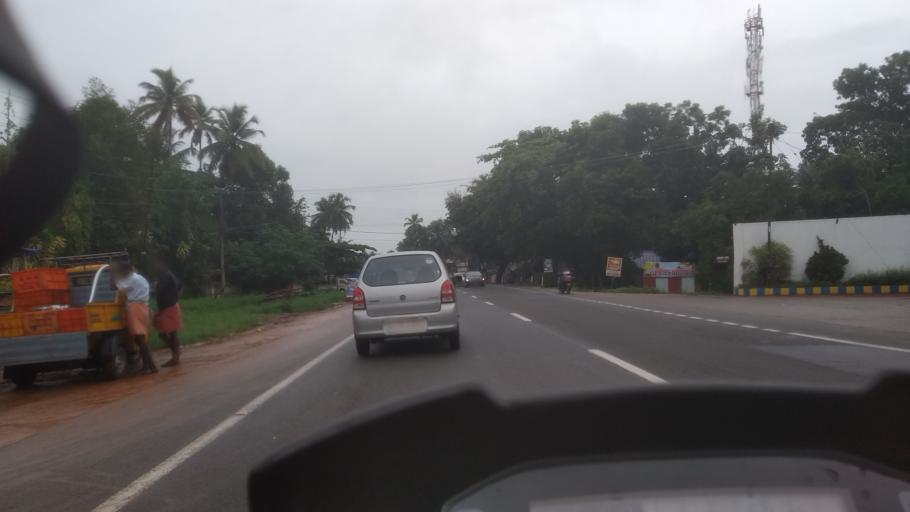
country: IN
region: Kerala
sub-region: Alappuzha
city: Kayankulam
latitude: 9.1571
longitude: 76.5091
